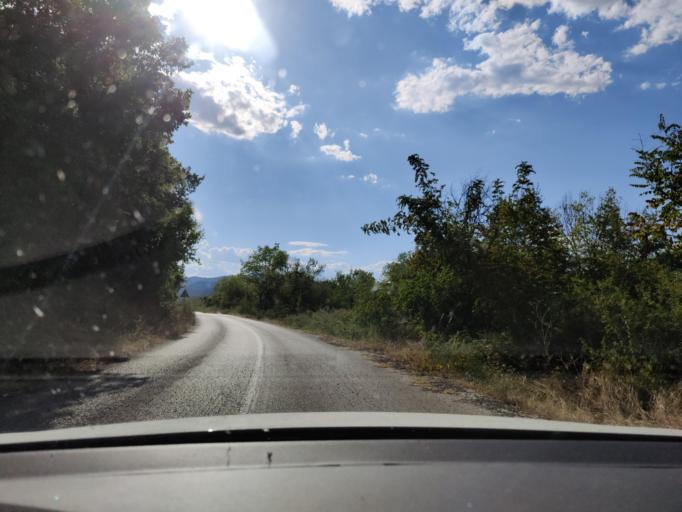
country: GR
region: Central Macedonia
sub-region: Nomos Serron
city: Chrysochorafa
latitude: 41.1796
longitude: 23.1404
